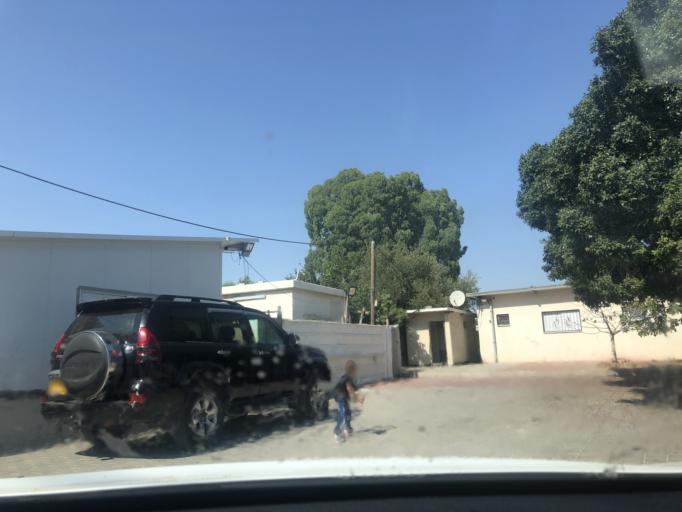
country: IL
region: Central District
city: Lod
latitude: 31.9589
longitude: 34.8961
